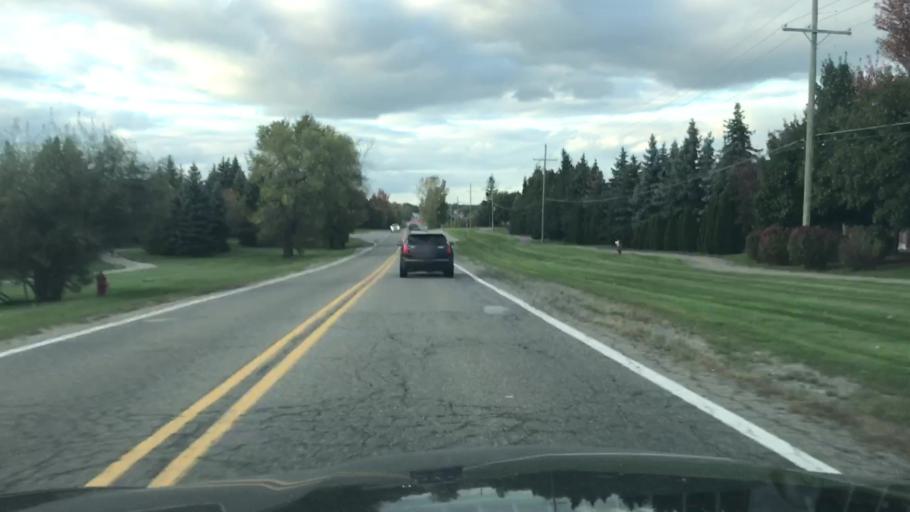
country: US
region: Michigan
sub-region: Oakland County
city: Rochester
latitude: 42.6915
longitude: -83.0946
